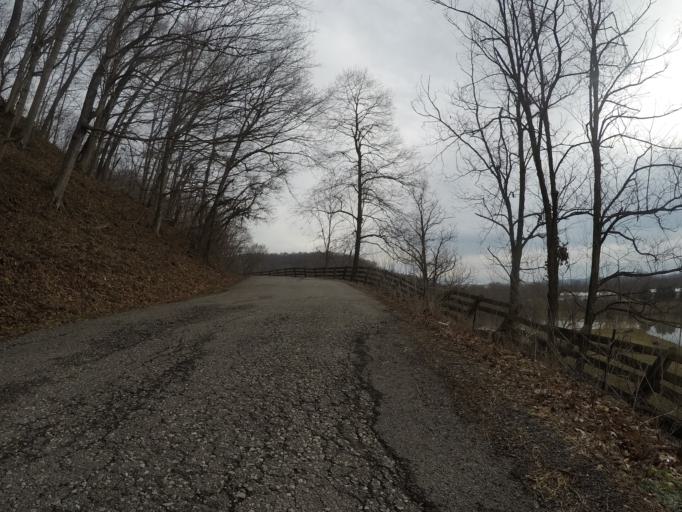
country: US
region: West Virginia
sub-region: Cabell County
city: Huntington
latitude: 38.4390
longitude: -82.4630
